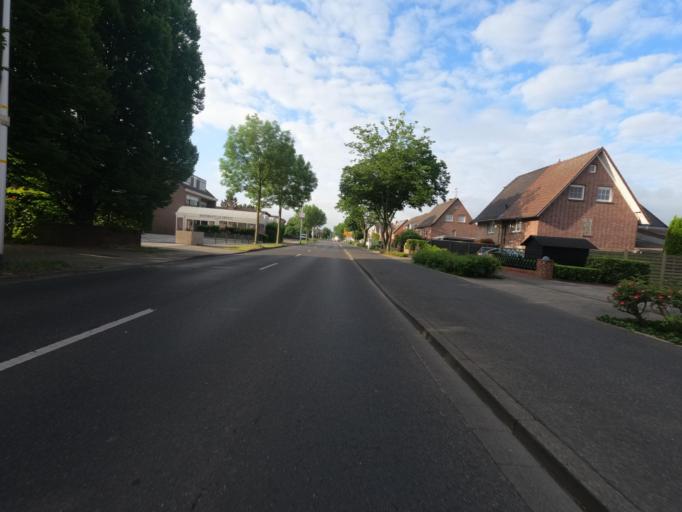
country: DE
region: North Rhine-Westphalia
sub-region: Regierungsbezirk Koln
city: Heinsberg
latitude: 51.0711
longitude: 6.0987
